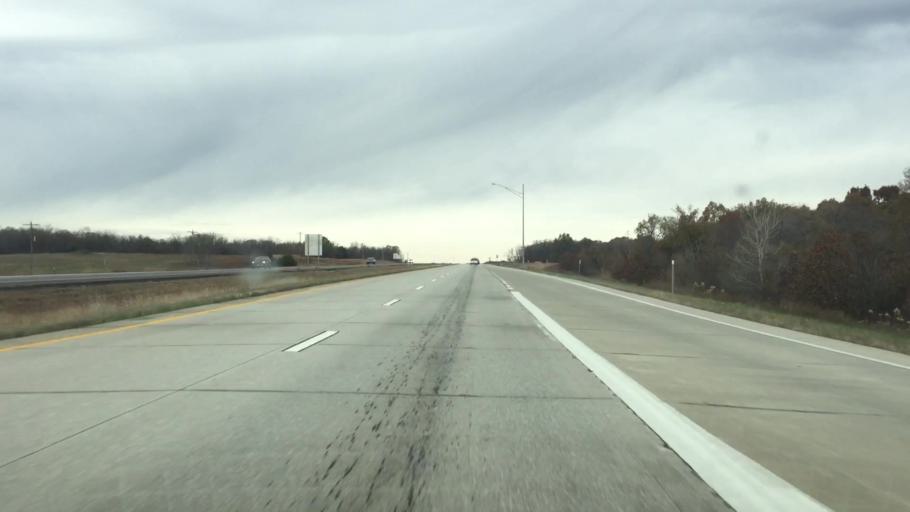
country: US
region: Missouri
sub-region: Saint Clair County
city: Osceola
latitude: 38.0431
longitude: -93.6827
